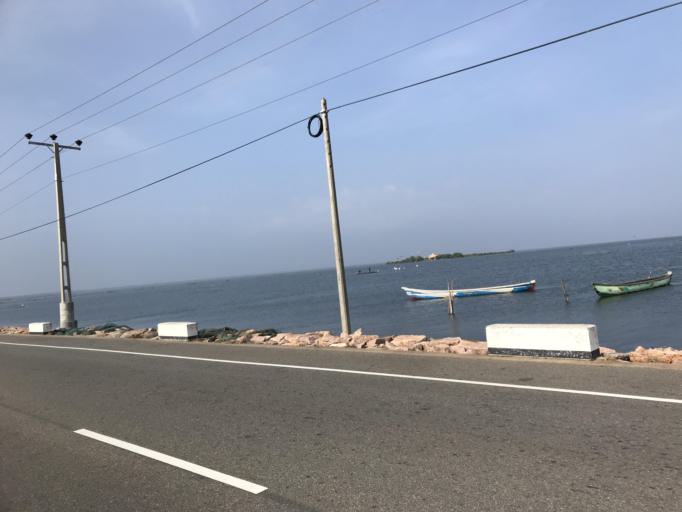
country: LK
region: Northern Province
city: Jaffna
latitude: 9.6539
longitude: 79.9978
